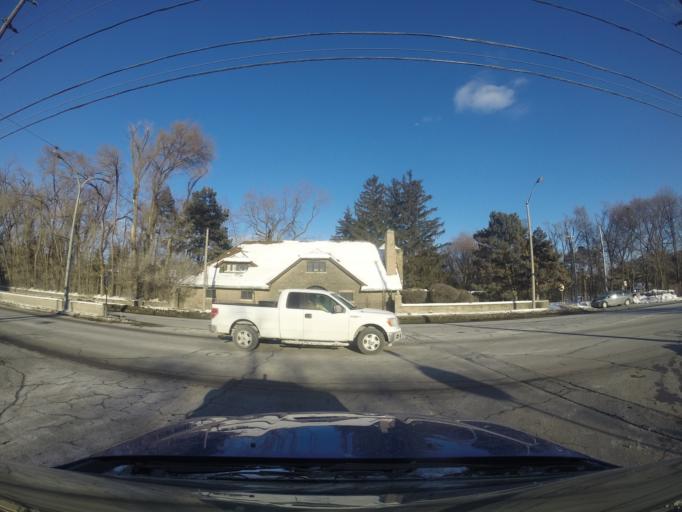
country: CA
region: Ontario
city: Toronto
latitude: 43.7246
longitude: -79.3798
